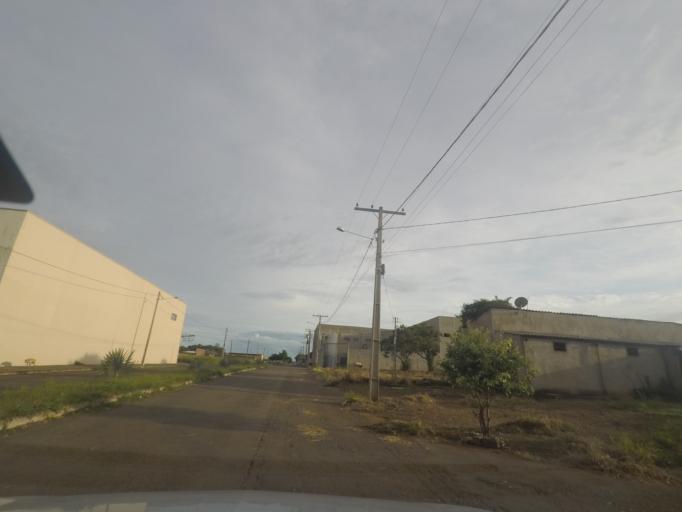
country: BR
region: Goias
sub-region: Trindade
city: Trindade
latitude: -16.7267
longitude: -49.4394
